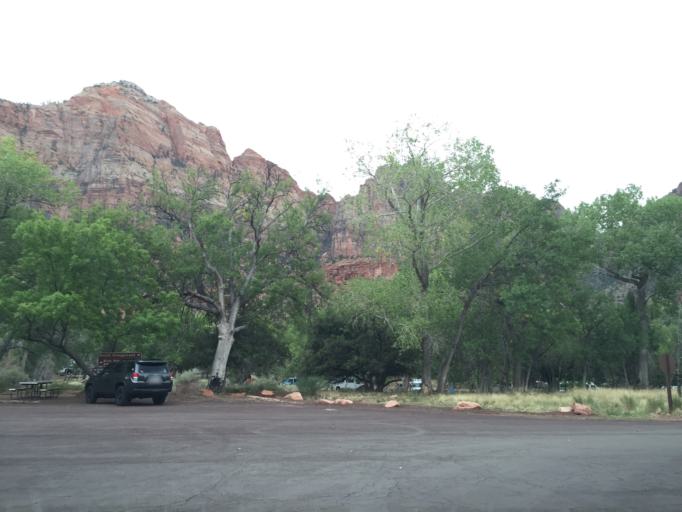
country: US
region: Utah
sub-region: Washington County
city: Hildale
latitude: 37.2047
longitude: -112.9835
